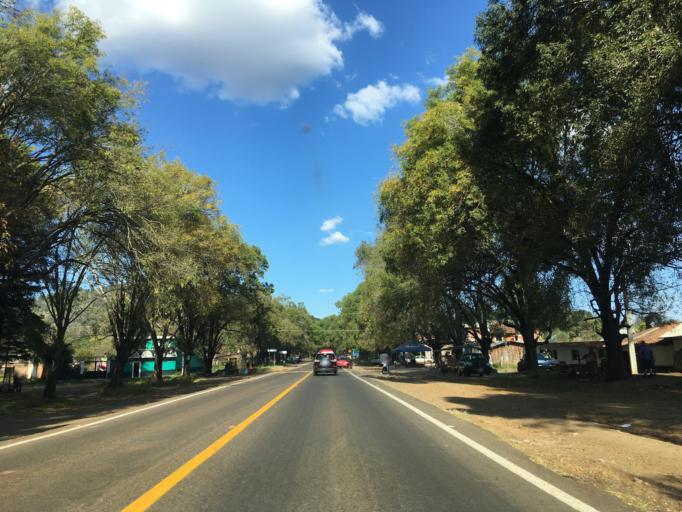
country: MX
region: Michoacan
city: Patzcuaro
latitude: 19.5479
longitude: -101.5827
